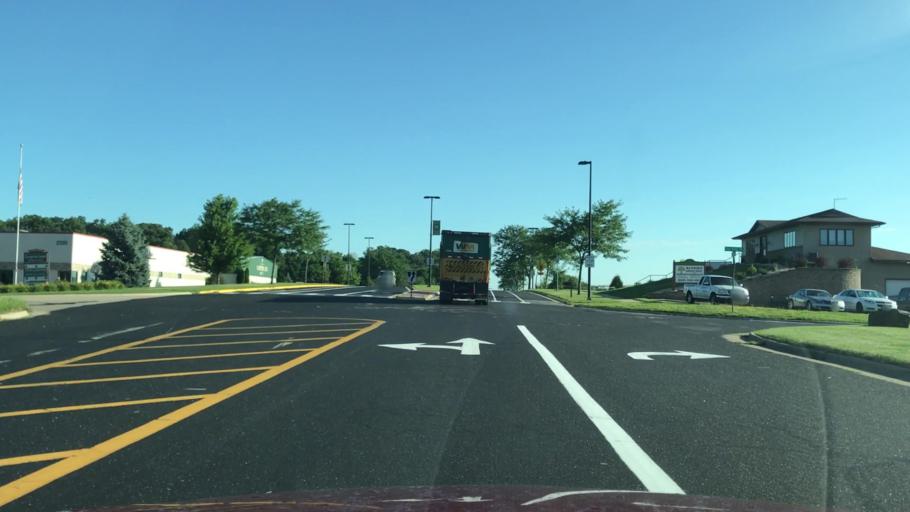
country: US
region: Wisconsin
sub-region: Dane County
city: Middleton
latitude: 43.1029
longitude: -89.5362
